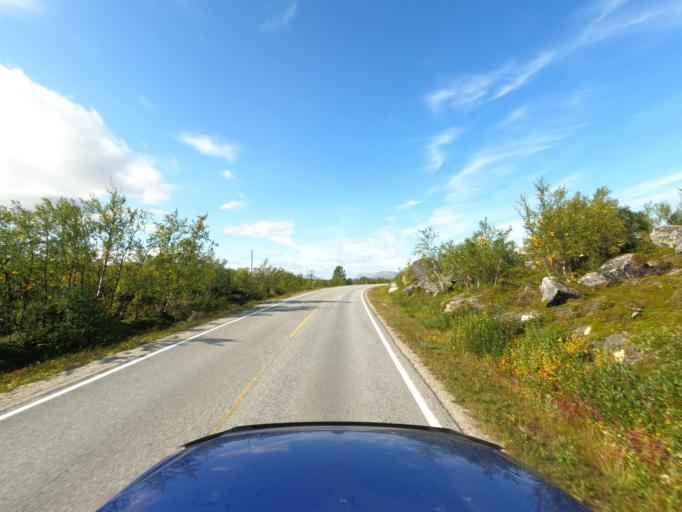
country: NO
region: Finnmark Fylke
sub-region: Porsanger
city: Lakselv
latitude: 69.7649
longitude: 25.1815
